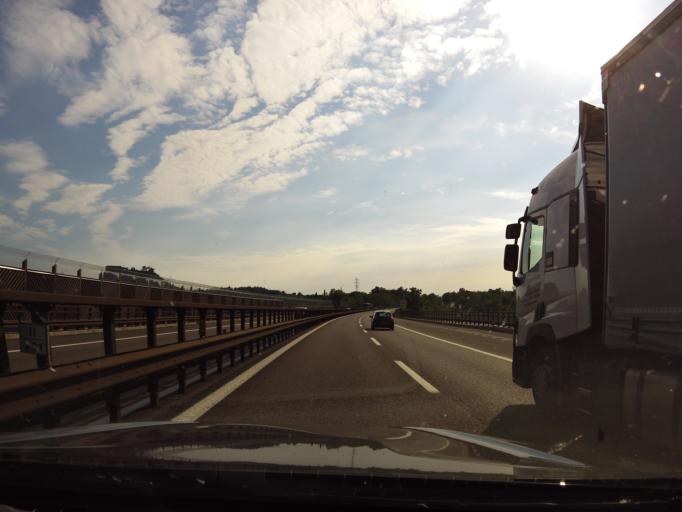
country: IT
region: Veneto
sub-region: Provincia di Verona
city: Rivoli Veronese
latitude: 45.5843
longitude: 10.8293
